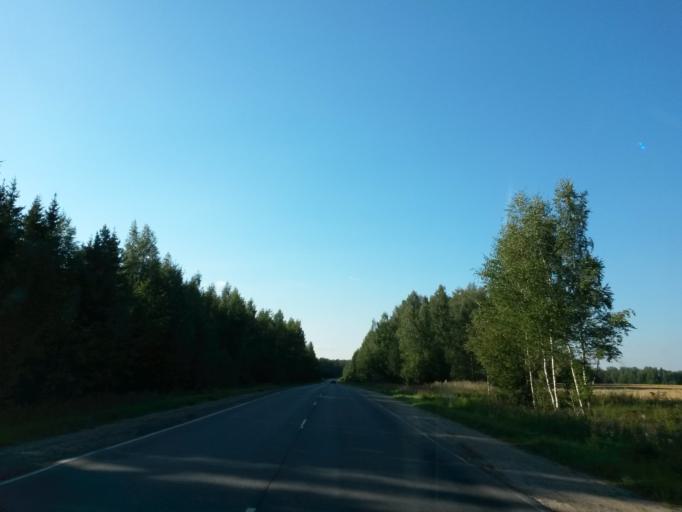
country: RU
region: Ivanovo
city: Pistsovo
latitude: 57.0973
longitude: 40.6582
